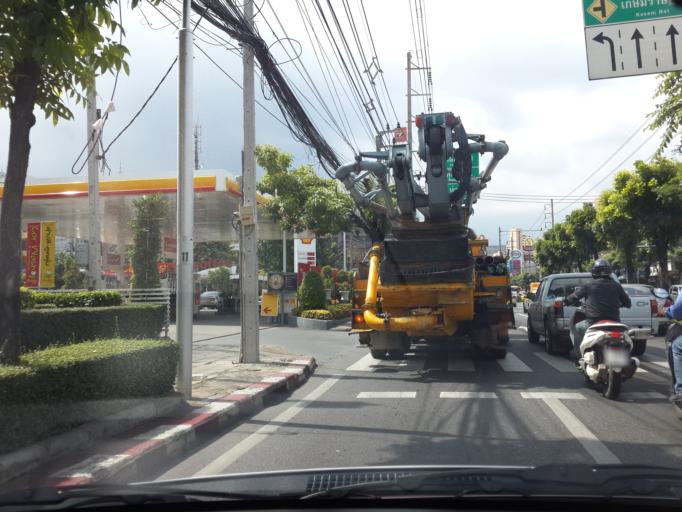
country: TH
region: Bangkok
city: Khlong Toei
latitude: 13.7187
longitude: 100.5678
